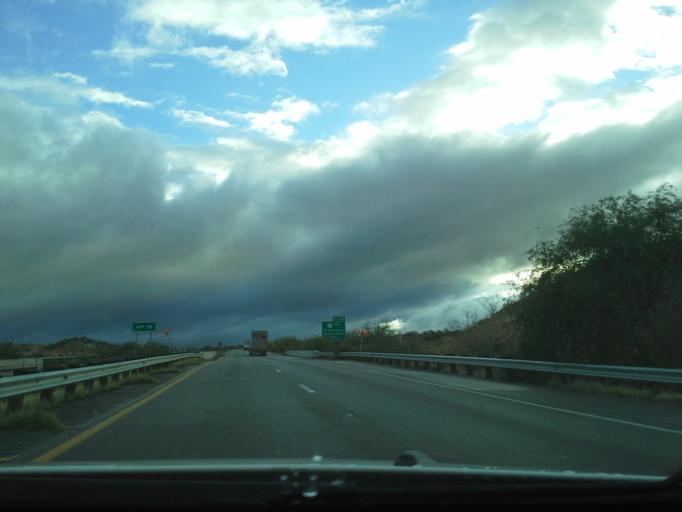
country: US
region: Arizona
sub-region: Cochise County
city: Whetstone
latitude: 31.9737
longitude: -110.3228
